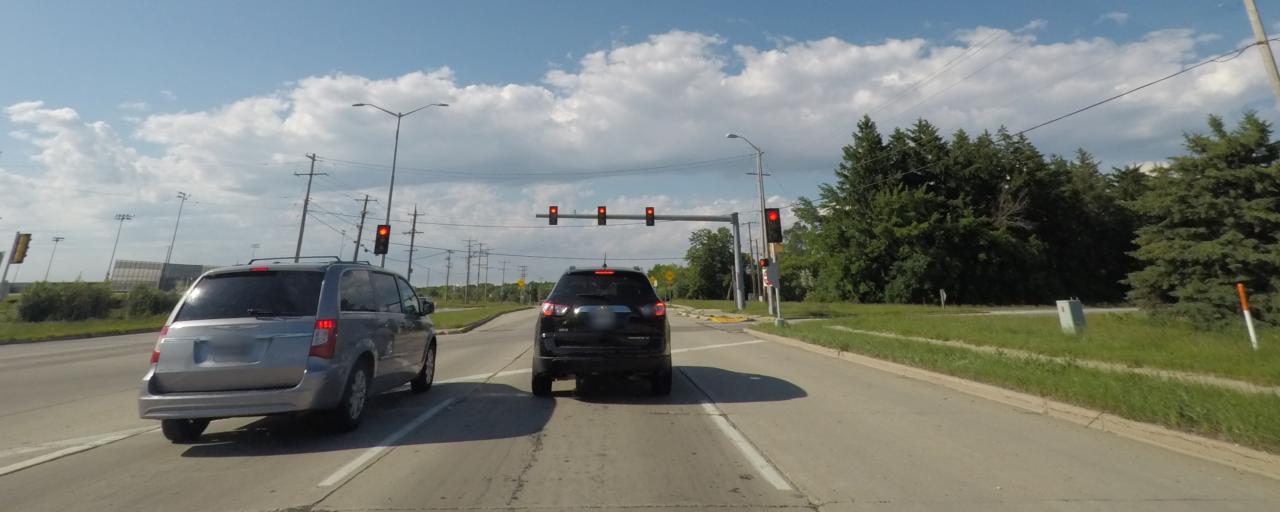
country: US
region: Wisconsin
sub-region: Milwaukee County
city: Greendale
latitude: 42.9196
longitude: -88.0090
